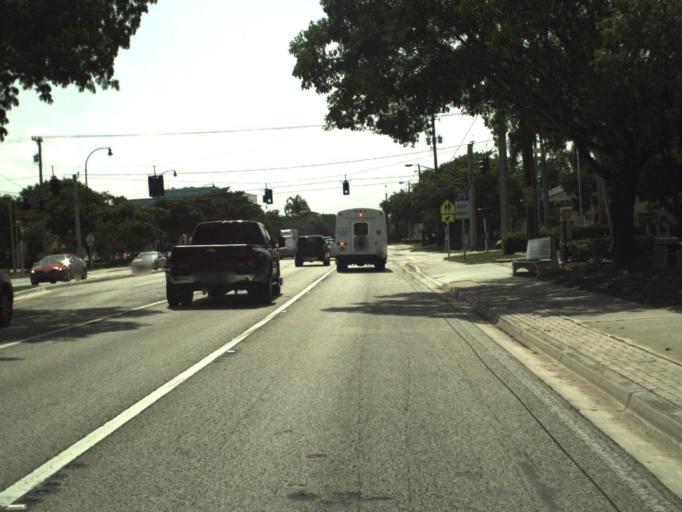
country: US
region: Florida
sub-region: Broward County
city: Deerfield Beach
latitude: 26.3187
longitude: -80.1071
